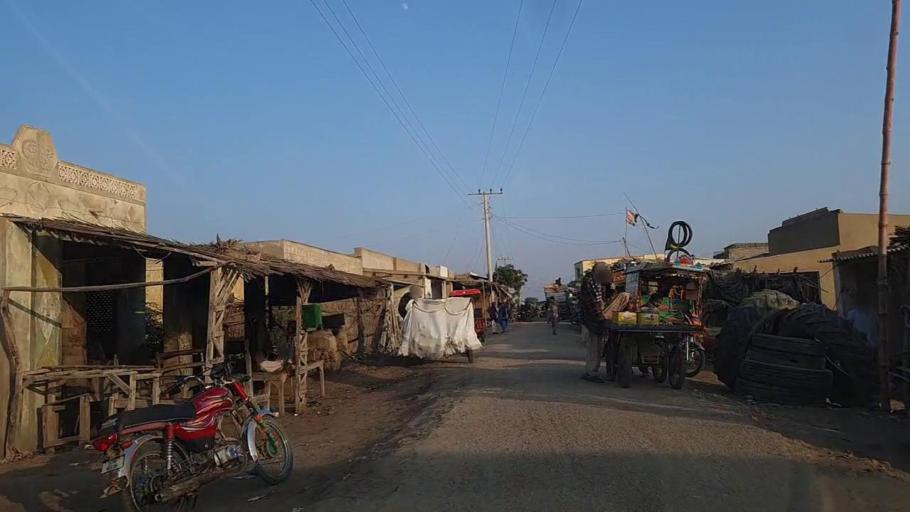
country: PK
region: Sindh
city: Keti Bandar
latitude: 24.2740
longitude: 67.6727
